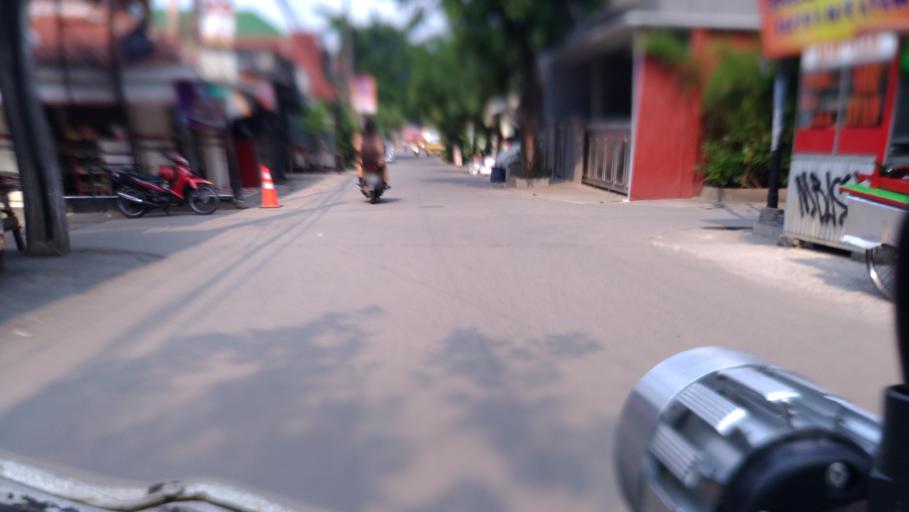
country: ID
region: West Java
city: Depok
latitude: -6.3621
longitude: 106.8737
